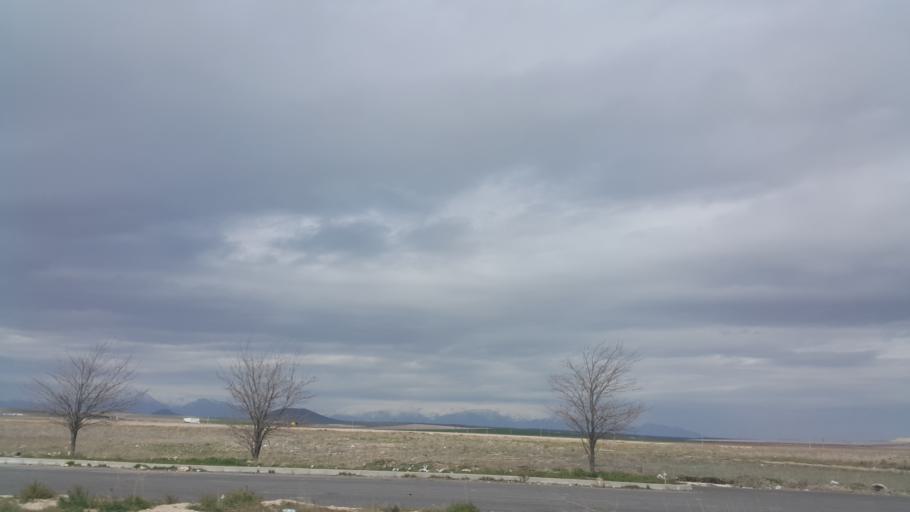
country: TR
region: Nigde
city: Altunhisar
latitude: 37.8712
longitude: 34.1573
